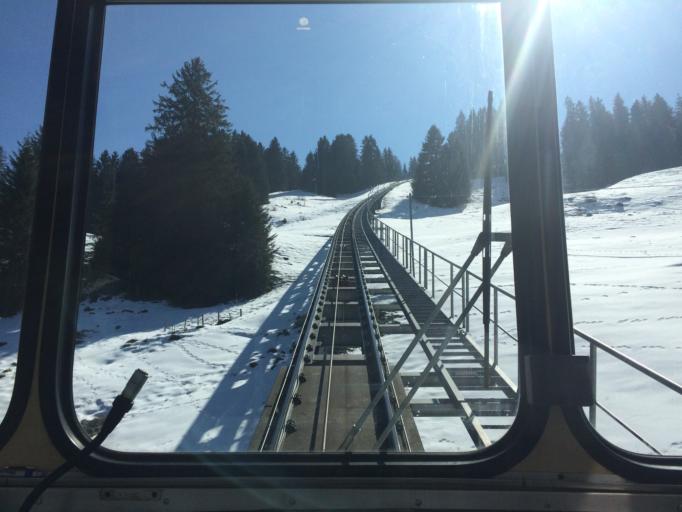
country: CH
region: Saint Gallen
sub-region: Wahlkreis Toggenburg
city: Wildhaus
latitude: 47.1923
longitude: 9.3114
